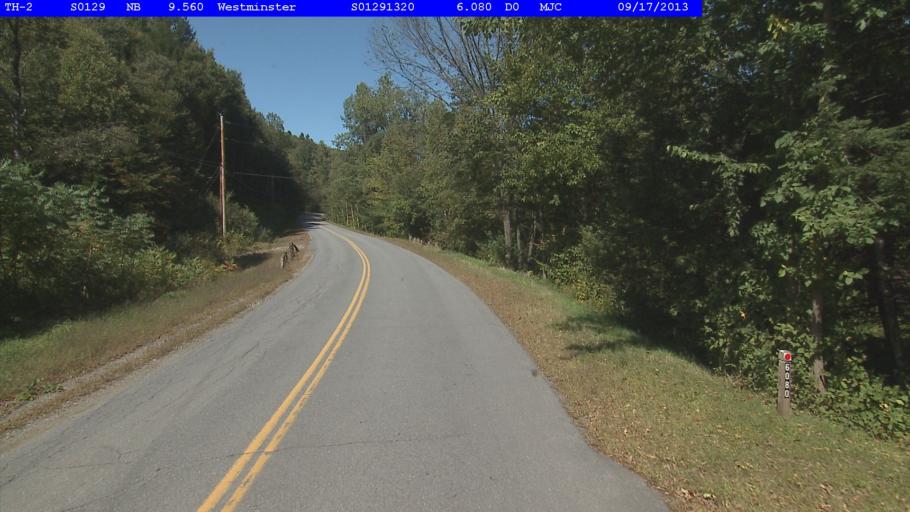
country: US
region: Vermont
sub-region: Windham County
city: Bellows Falls
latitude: 43.1023
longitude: -72.5363
